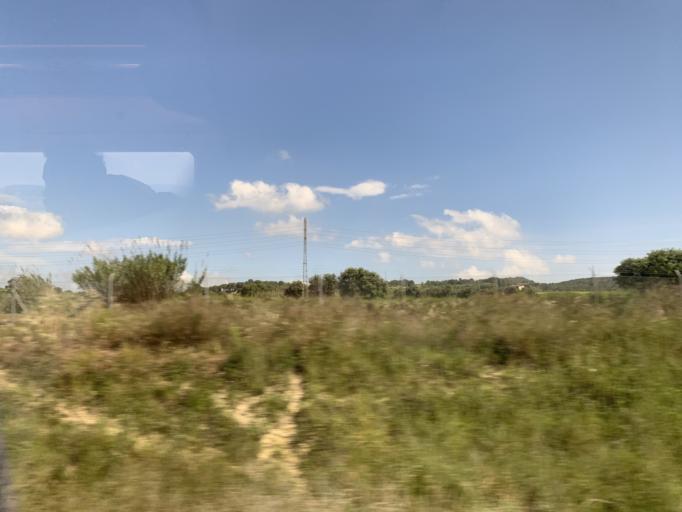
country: ES
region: Catalonia
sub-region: Provincia de Barcelona
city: Vilafranca del Penedes
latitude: 41.3243
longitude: 1.6807
